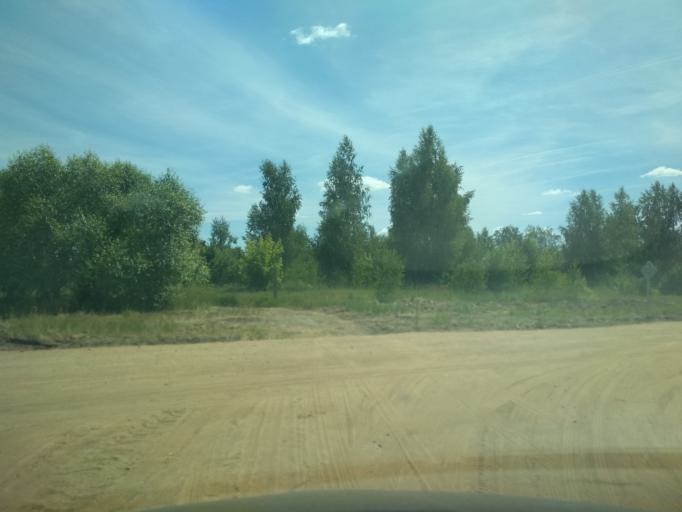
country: BY
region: Minsk
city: Mar''ina Horka
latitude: 53.5100
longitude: 28.1646
